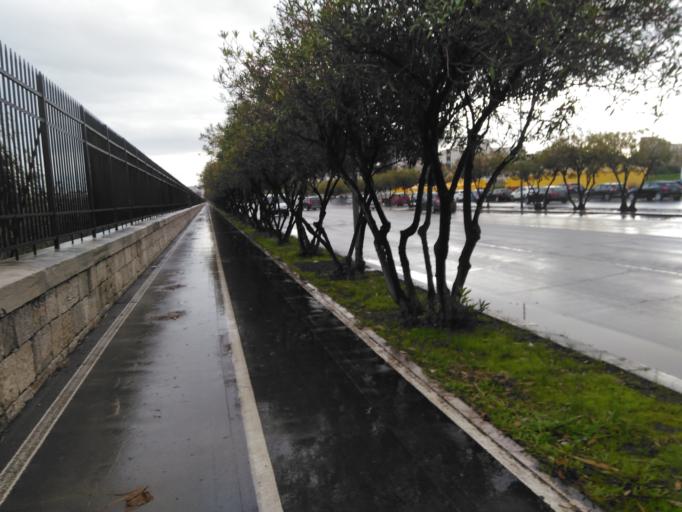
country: IT
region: Apulia
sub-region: Provincia di Bari
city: Bari
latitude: 41.1321
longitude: 16.8470
